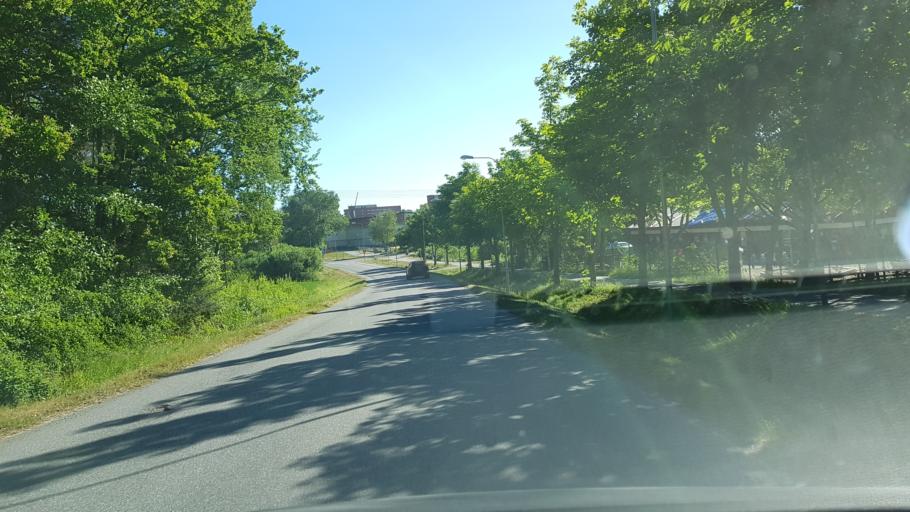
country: SE
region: Stockholm
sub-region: Jarfalla Kommun
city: Jakobsberg
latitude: 59.4153
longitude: 17.8212
